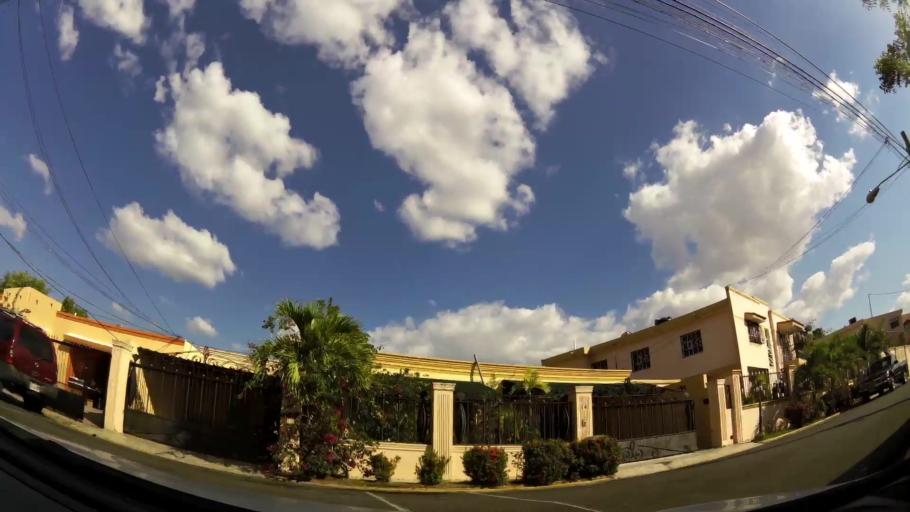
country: DO
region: Nacional
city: Santo Domingo
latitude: 18.5116
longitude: -69.9863
